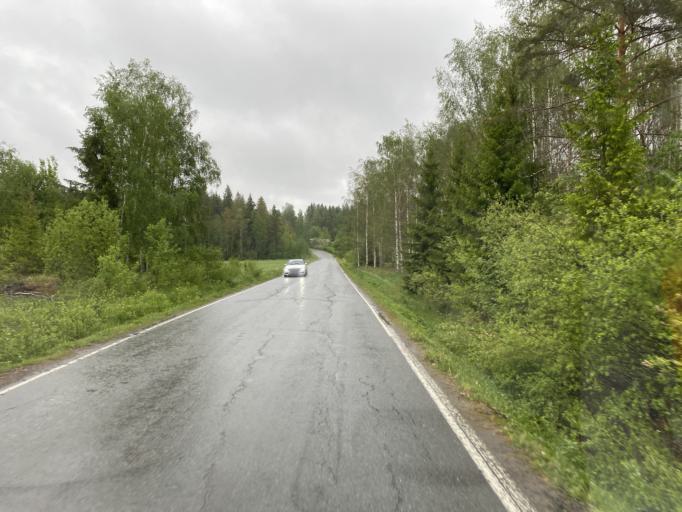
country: FI
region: Pirkanmaa
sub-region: Etelae-Pirkanmaa
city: Urjala
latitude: 60.9667
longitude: 23.5219
